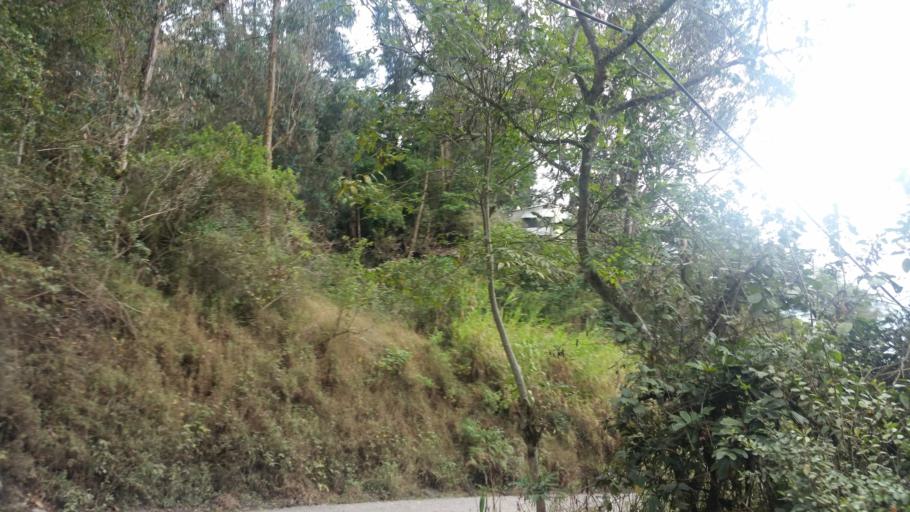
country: CO
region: Cundinamarca
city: Choachi
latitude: 4.5127
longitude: -73.9318
